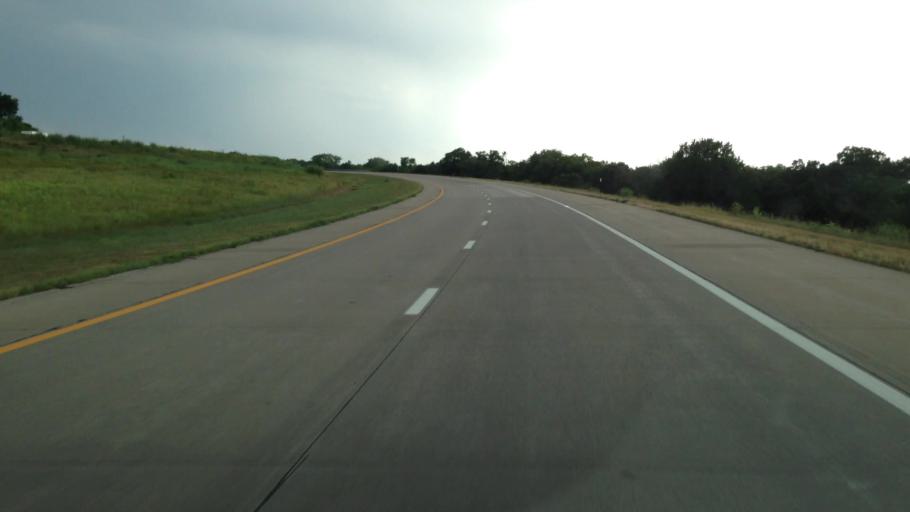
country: US
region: Kansas
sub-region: Osage County
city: Lyndon
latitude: 38.4728
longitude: -95.5227
